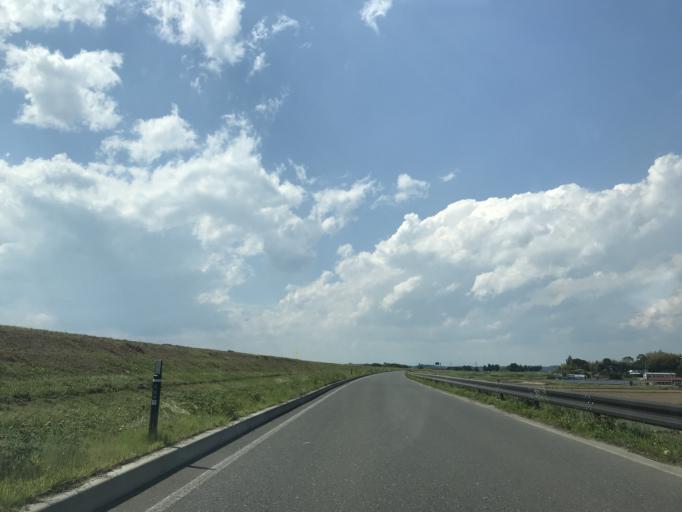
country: JP
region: Miyagi
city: Matsushima
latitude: 38.4353
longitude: 141.1198
